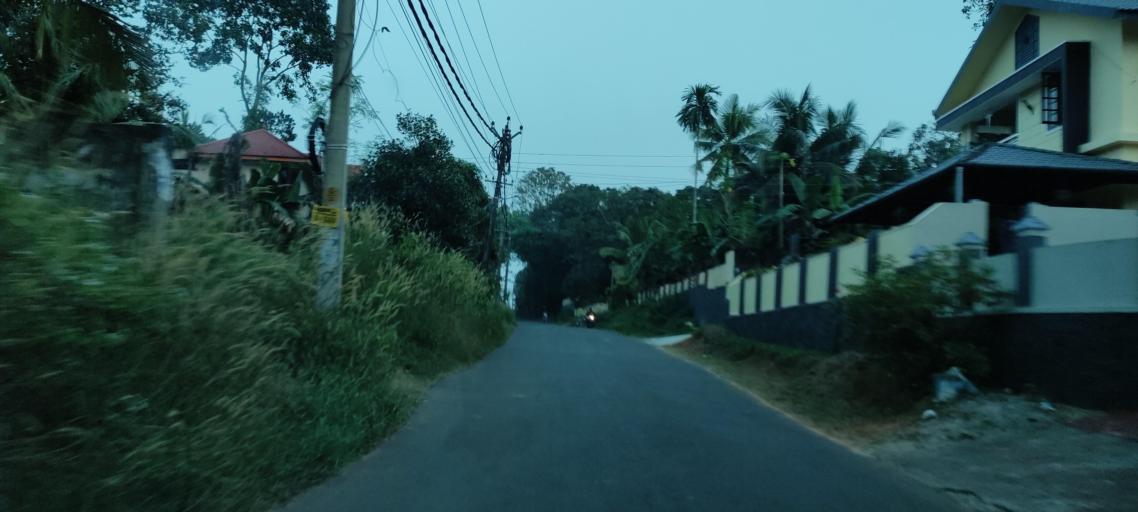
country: IN
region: Kerala
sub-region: Pattanamtitta
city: Adur
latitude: 9.1607
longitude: 76.7463
